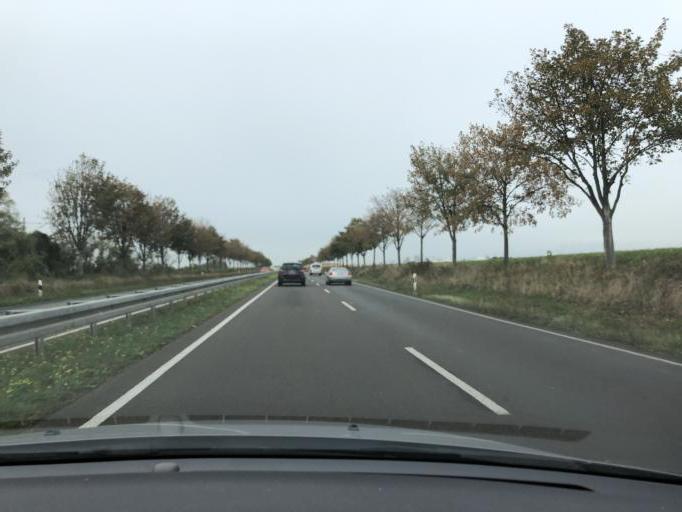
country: DE
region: Saxony
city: Schkeuditz
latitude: 51.4000
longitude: 12.2648
